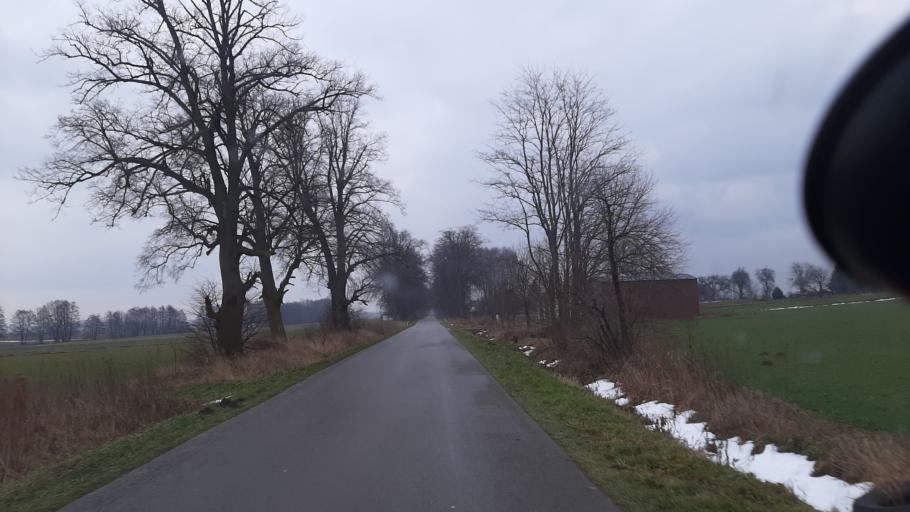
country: PL
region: Lublin Voivodeship
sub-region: Powiat lubelski
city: Jastkow
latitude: 51.3477
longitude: 22.5190
